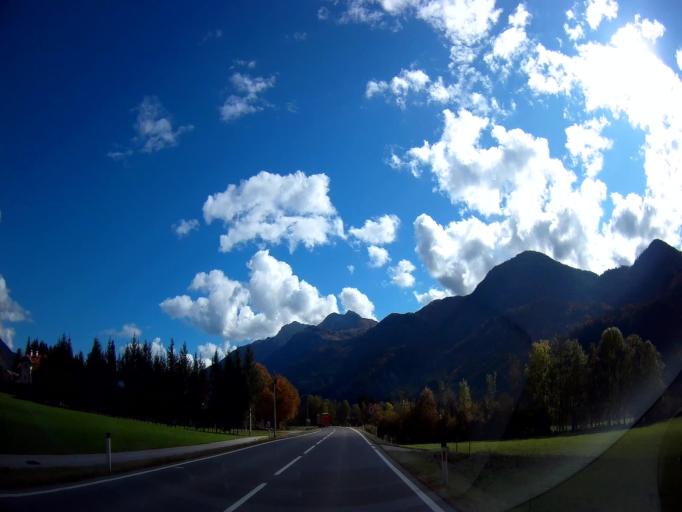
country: AT
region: Carinthia
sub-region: Politischer Bezirk Spittal an der Drau
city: Oberdrauburg
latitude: 46.7483
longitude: 12.9911
